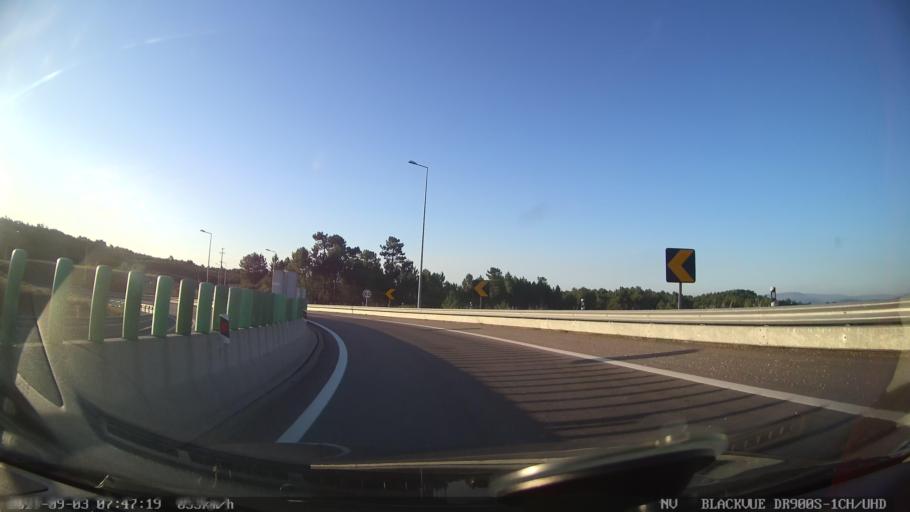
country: PT
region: Vila Real
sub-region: Vila Real
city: Vila Real
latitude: 41.2947
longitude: -7.6955
